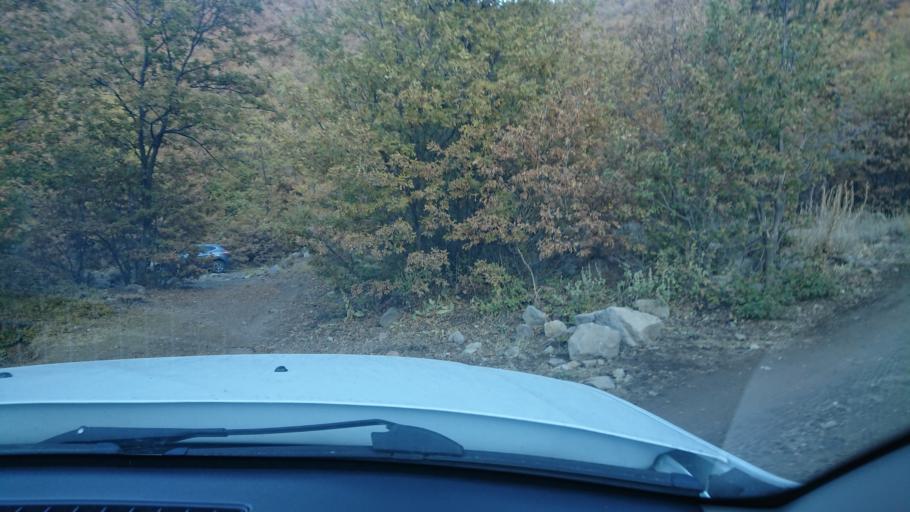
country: TR
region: Aksaray
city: Taspinar
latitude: 38.1645
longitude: 34.2101
